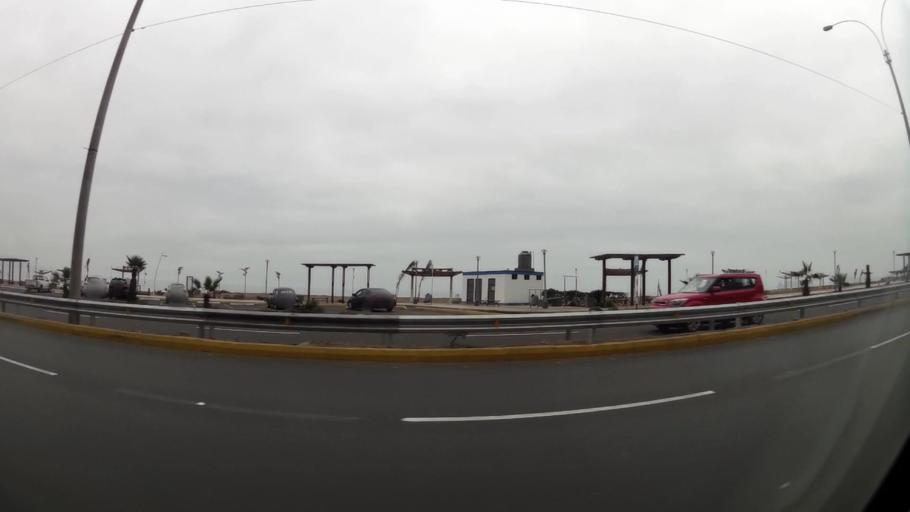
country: PE
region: Lima
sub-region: Lima
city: San Isidro
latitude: -12.0928
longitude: -77.0826
